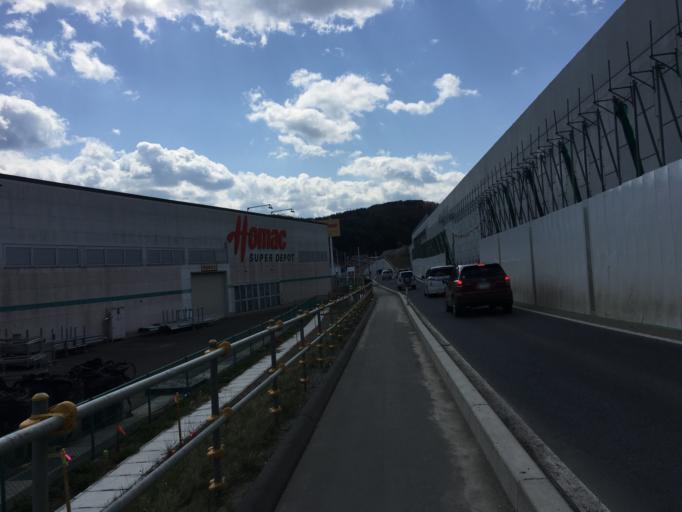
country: JP
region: Aomori
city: Hachinohe
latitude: 40.1902
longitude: 141.7873
